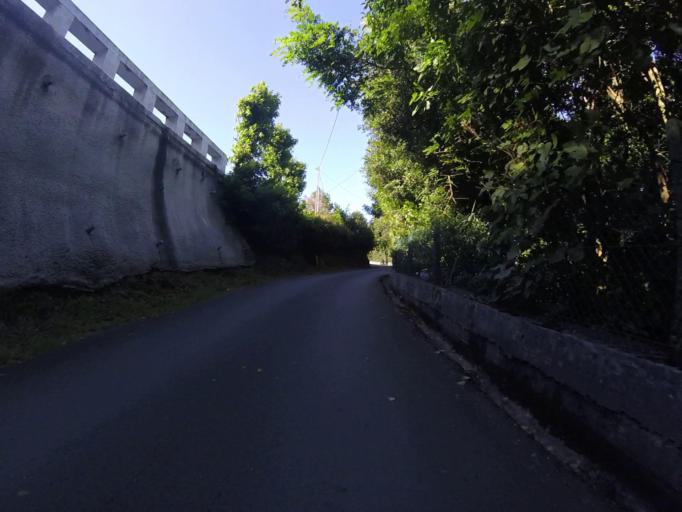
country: ES
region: Basque Country
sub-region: Provincia de Guipuzcoa
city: Fuenterrabia
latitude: 43.3894
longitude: -1.7914
